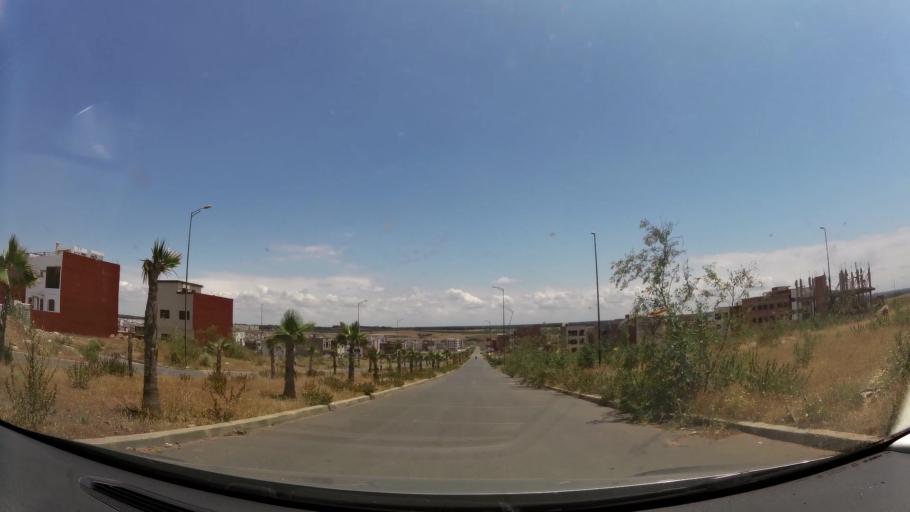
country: MA
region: Gharb-Chrarda-Beni Hssen
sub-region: Kenitra Province
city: Kenitra
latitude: 34.2486
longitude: -6.6608
